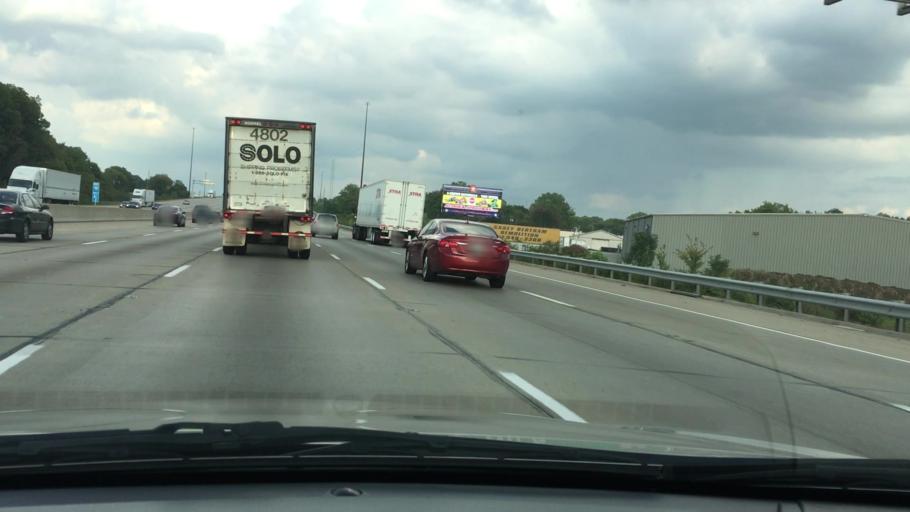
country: US
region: Indiana
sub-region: Marion County
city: Warren Park
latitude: 39.8042
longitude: -86.0715
